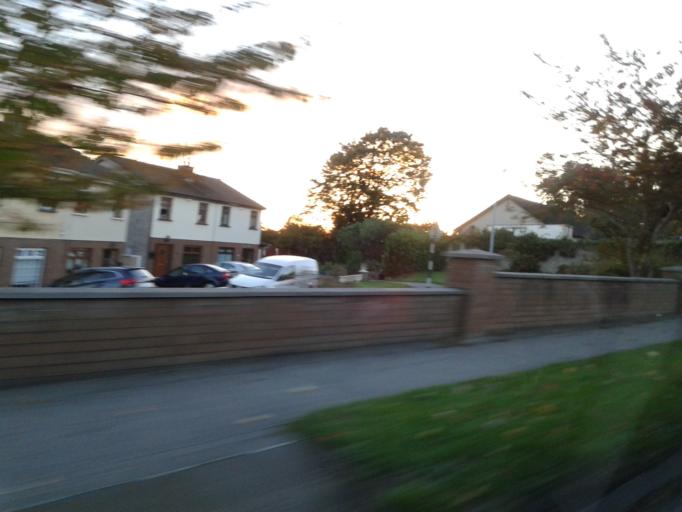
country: IE
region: Leinster
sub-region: Lu
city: Drogheda
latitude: 53.7195
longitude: -6.3751
